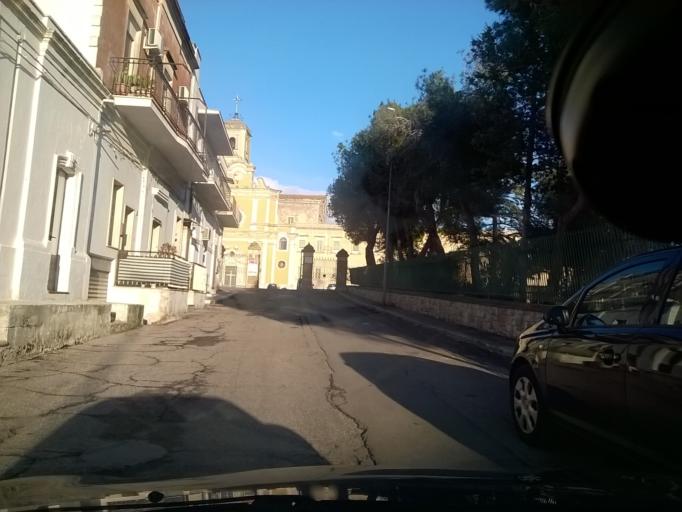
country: IT
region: Apulia
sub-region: Provincia di Brindisi
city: Oria
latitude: 40.4960
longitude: 17.6491
